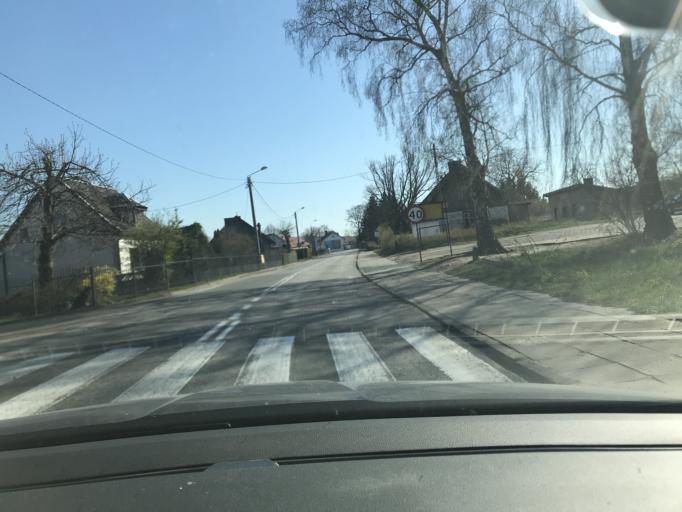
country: PL
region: Pomeranian Voivodeship
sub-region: Powiat nowodworski
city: Sztutowo
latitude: 54.3295
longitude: 19.1788
